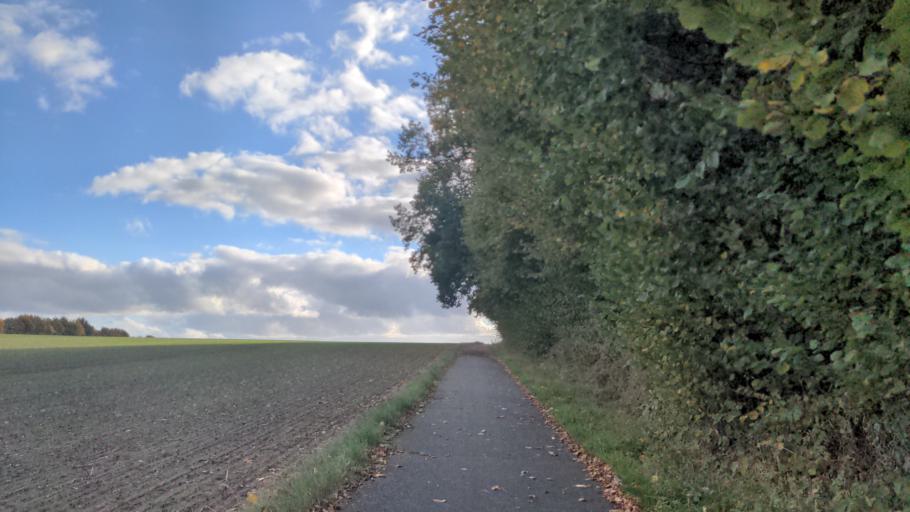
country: DE
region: Schleswig-Holstein
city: Bosau
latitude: 54.1174
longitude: 10.4435
